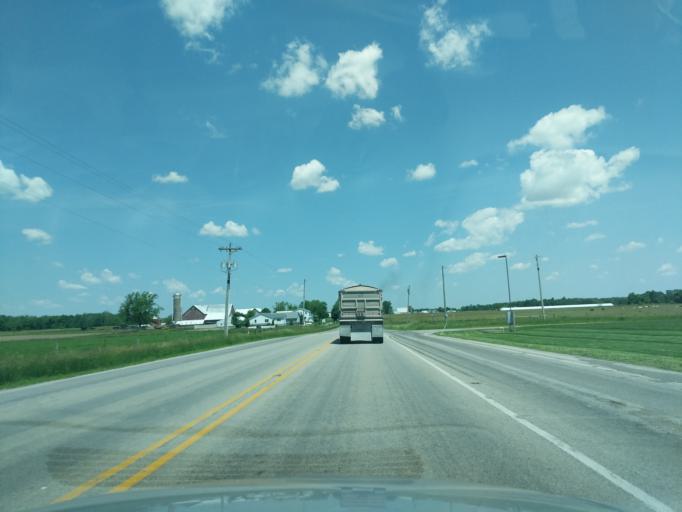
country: US
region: Indiana
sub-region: LaGrange County
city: Topeka
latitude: 41.6322
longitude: -85.5798
